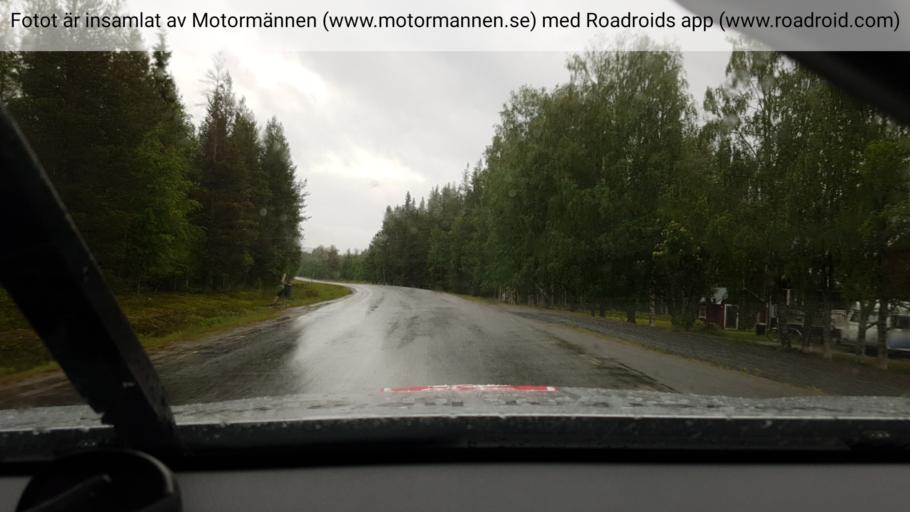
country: SE
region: Vaesterbotten
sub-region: Mala Kommun
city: Mala
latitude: 65.2031
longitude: 18.6897
